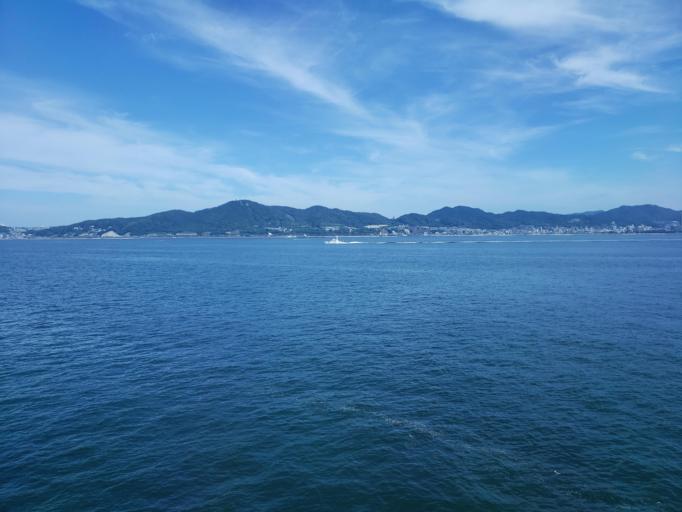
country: JP
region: Hyogo
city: Kobe
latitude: 34.6124
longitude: 135.1159
